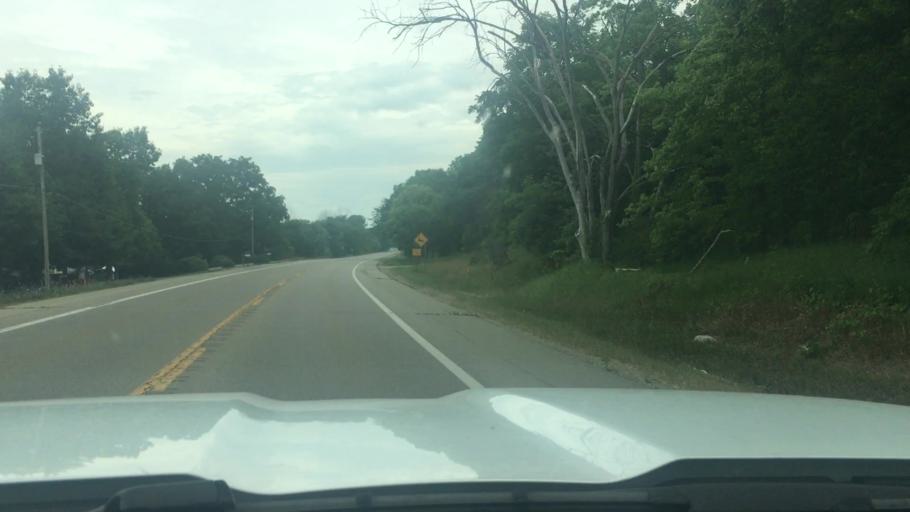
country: US
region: Michigan
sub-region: Ionia County
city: Saranac
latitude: 42.9318
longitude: -85.2508
